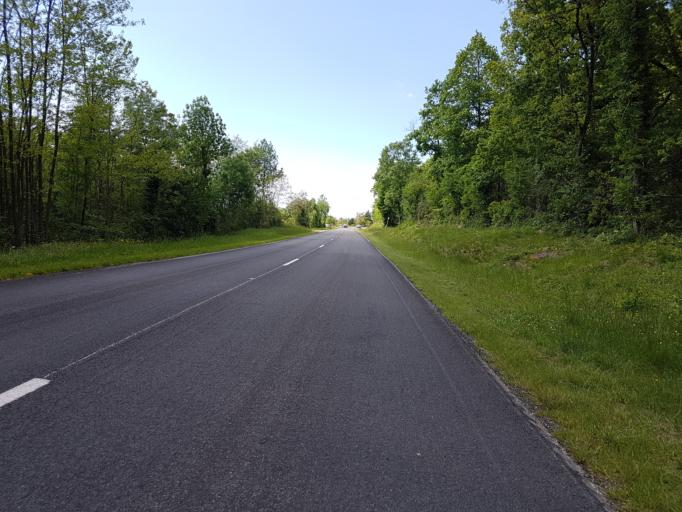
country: FR
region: Rhone-Alpes
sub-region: Departement de l'Isere
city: Bouvesse-Quirieu
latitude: 45.7863
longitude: 5.4650
